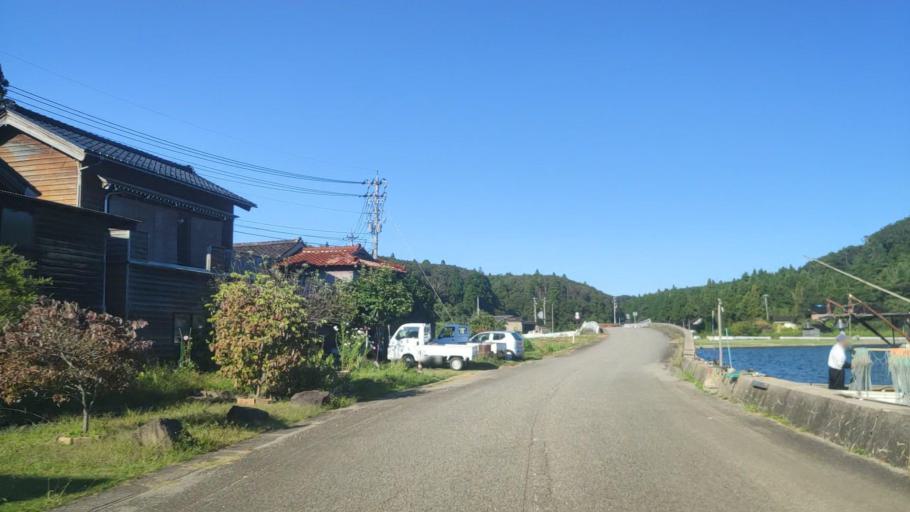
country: JP
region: Ishikawa
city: Nanao
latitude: 37.1144
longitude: 136.8822
